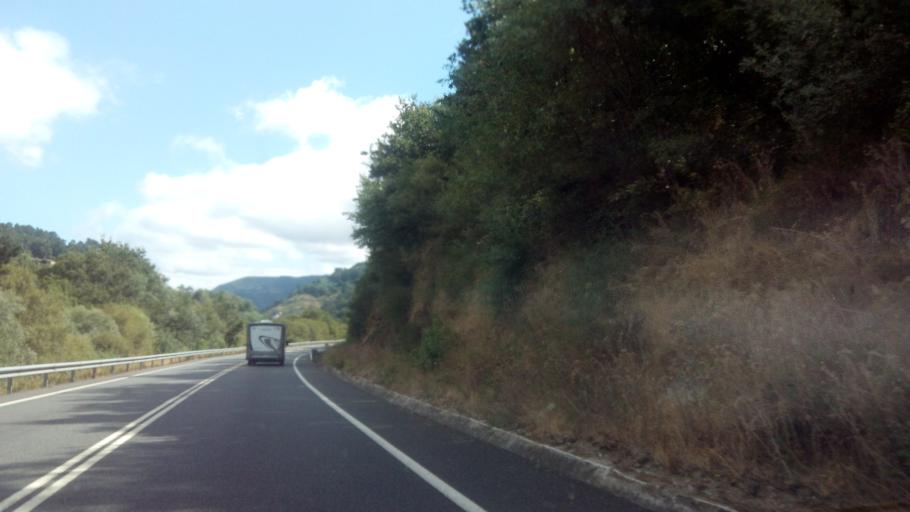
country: ES
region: Galicia
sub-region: Provincia de Ourense
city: Nogueira de Ramuin
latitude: 42.4264
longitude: -7.7620
